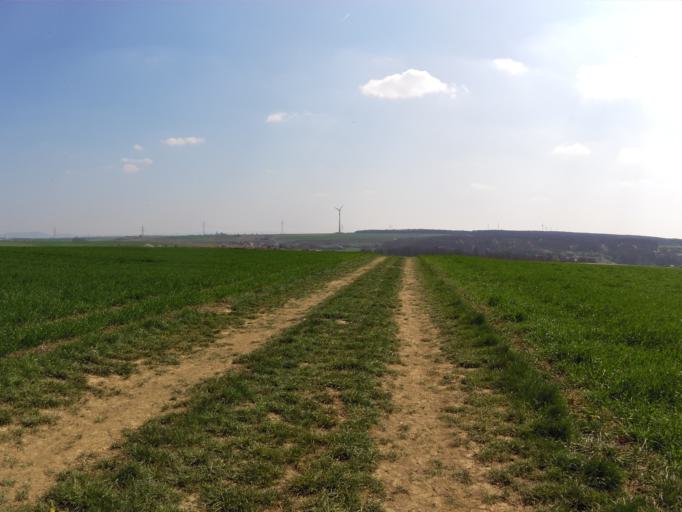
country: DE
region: Bavaria
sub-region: Regierungsbezirk Unterfranken
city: Theilheim
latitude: 49.7626
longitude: 10.0278
